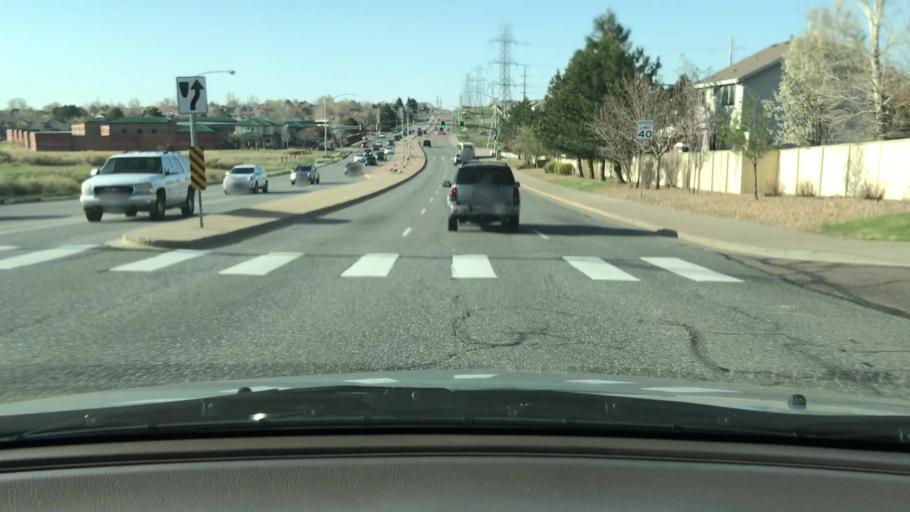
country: US
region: Colorado
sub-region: Adams County
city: Aurora
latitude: 39.6656
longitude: -104.7723
